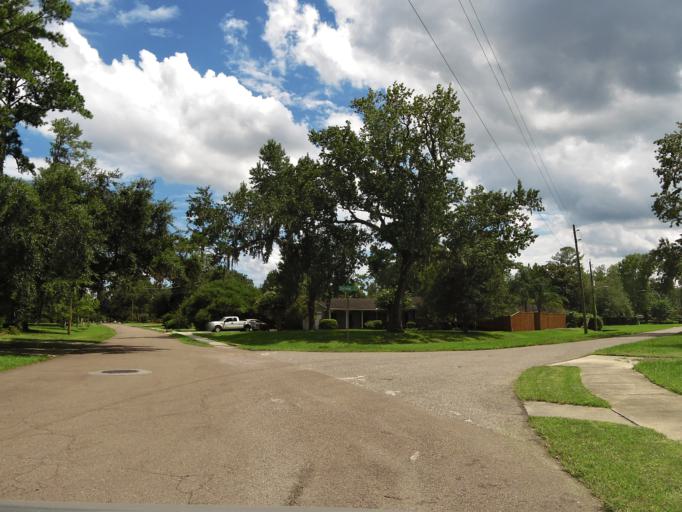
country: US
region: Florida
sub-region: Duval County
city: Jacksonville
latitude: 30.2691
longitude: -81.7134
